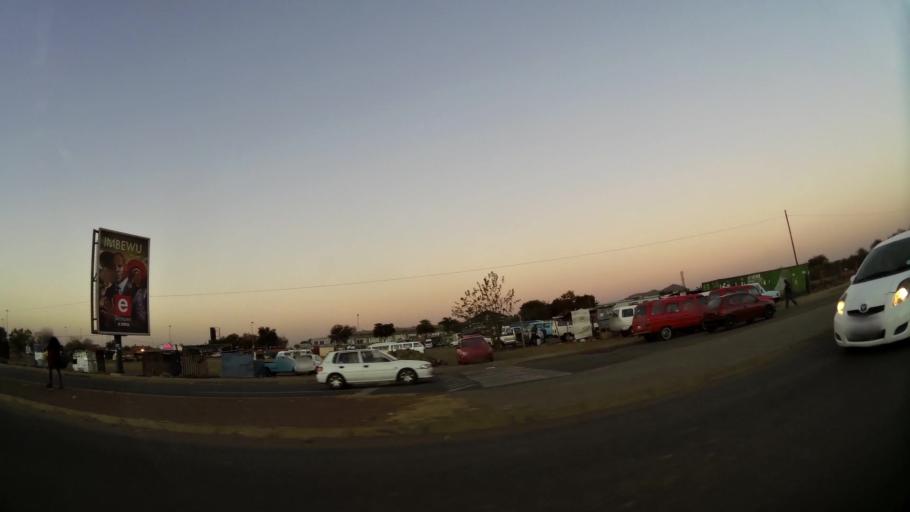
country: ZA
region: North-West
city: Ga-Rankuwa
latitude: -25.5906
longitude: 27.9894
